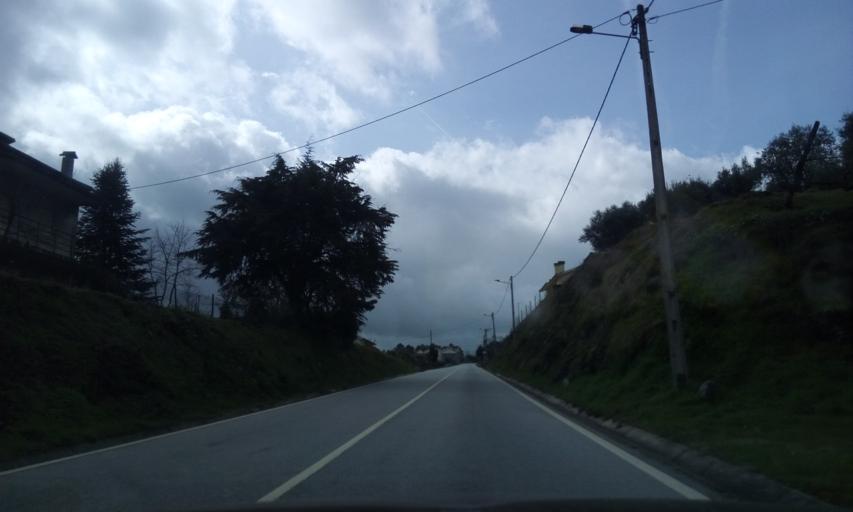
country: PT
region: Viseu
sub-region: Mangualde
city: Mangualde
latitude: 40.6320
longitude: -7.7473
